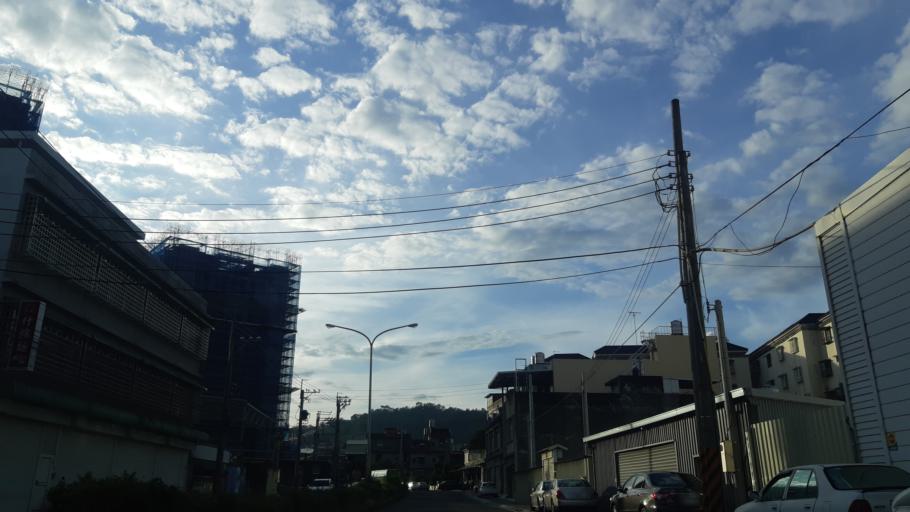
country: TW
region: Taiwan
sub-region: Hsinchu
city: Zhubei
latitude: 24.7307
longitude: 121.0954
